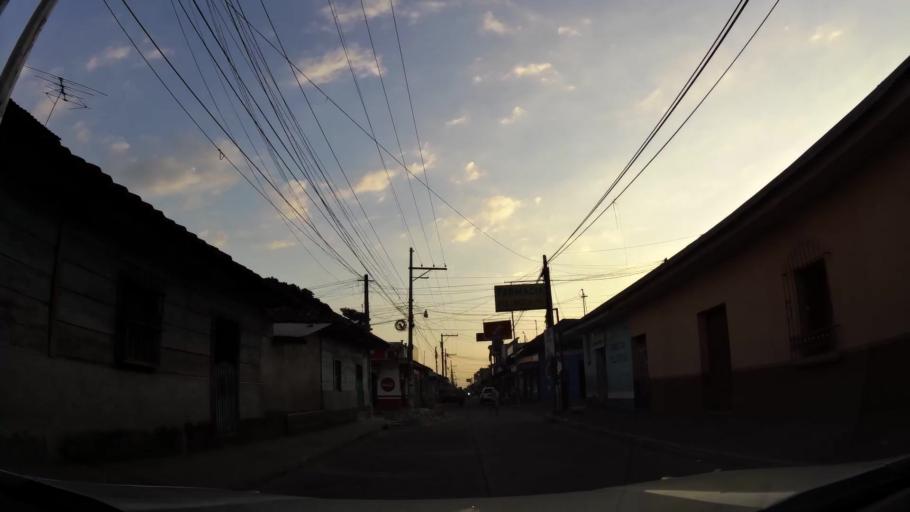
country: GT
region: Retalhuleu
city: San Sebastian
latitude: 14.5633
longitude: -91.6480
